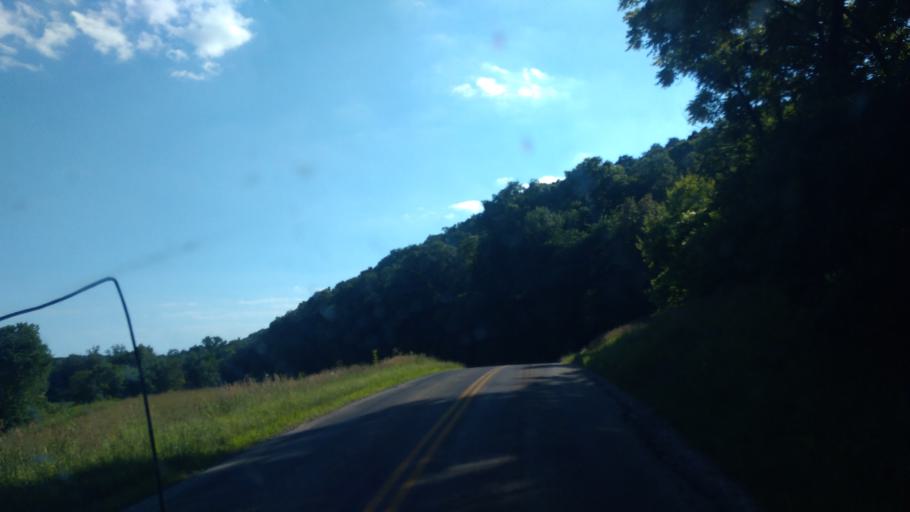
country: US
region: Ohio
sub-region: Ashland County
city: Loudonville
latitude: 40.7258
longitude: -82.1576
